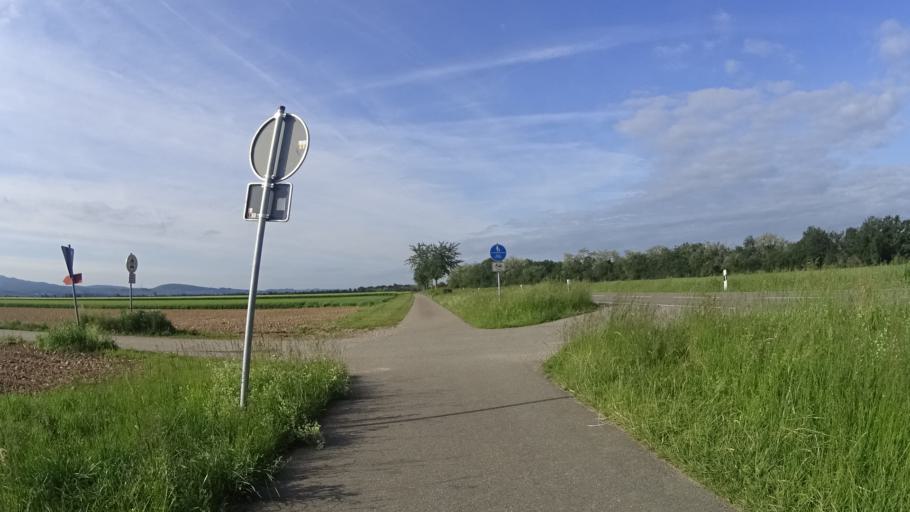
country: FR
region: Alsace
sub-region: Departement du Haut-Rhin
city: Blodelsheim
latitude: 47.8639
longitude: 7.5866
